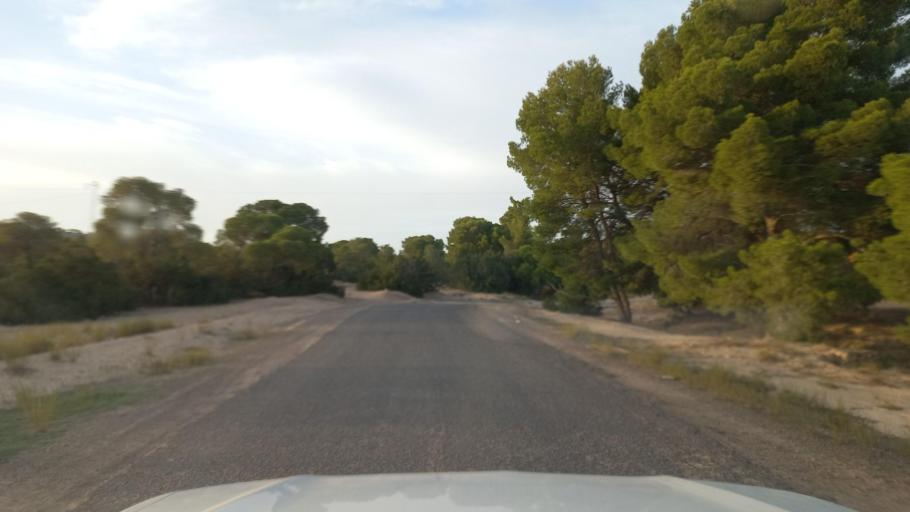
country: TN
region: Al Qasrayn
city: Sbiba
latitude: 35.4126
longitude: 8.9268
